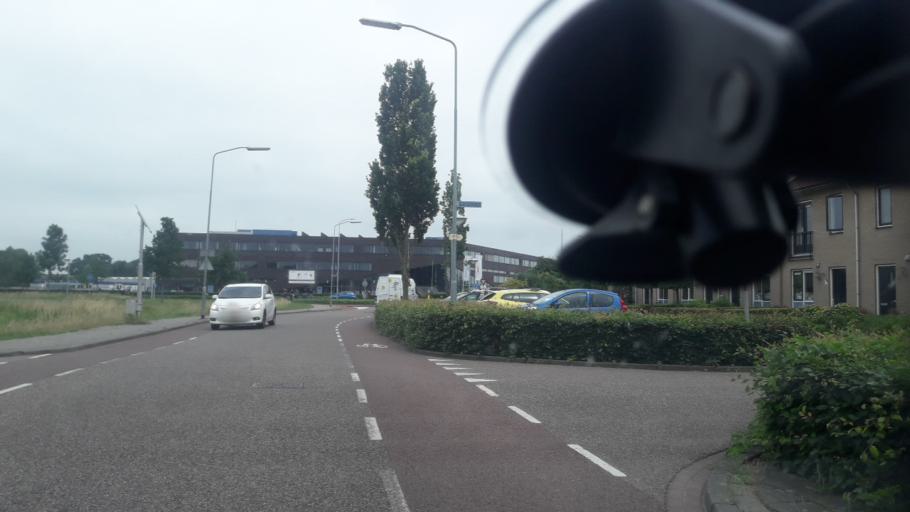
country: NL
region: Gelderland
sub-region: Gemeente Elburg
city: Elburg
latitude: 52.4477
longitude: 5.8638
